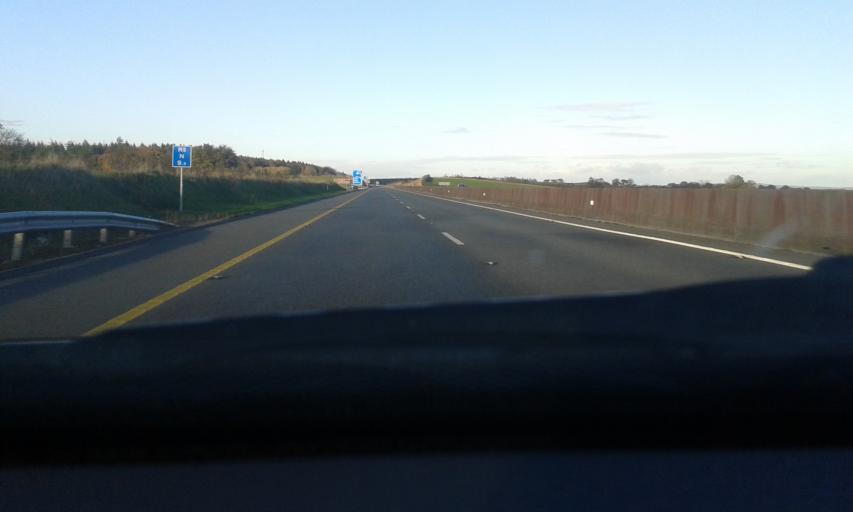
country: IE
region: Leinster
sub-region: Laois
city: Rathdowney
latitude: 52.8480
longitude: -7.4946
